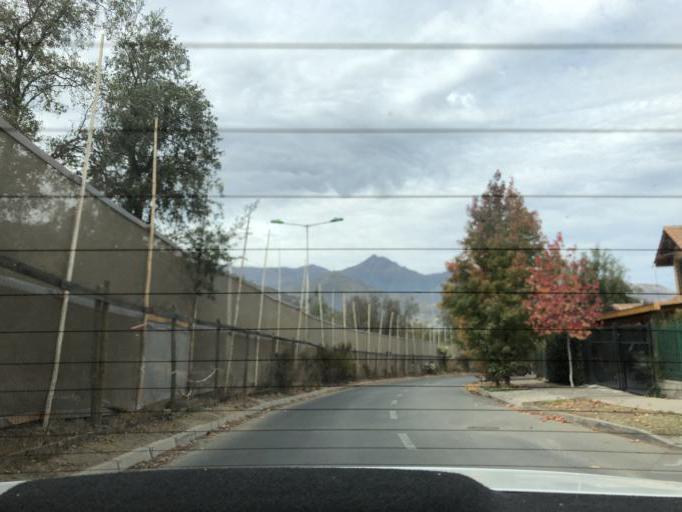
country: CL
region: Santiago Metropolitan
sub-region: Provincia de Cordillera
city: Puente Alto
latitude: -33.5836
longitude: -70.5062
